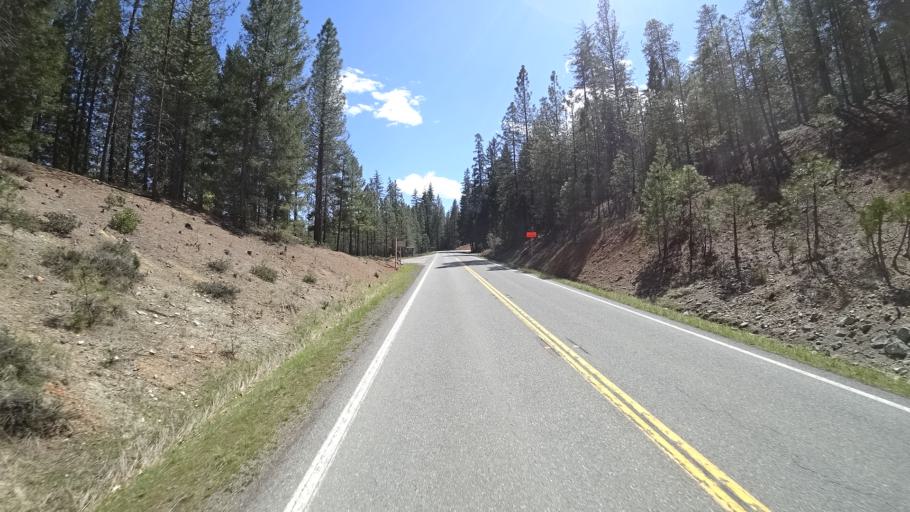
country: US
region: California
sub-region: Trinity County
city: Lewiston
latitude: 40.8618
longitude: -122.8174
